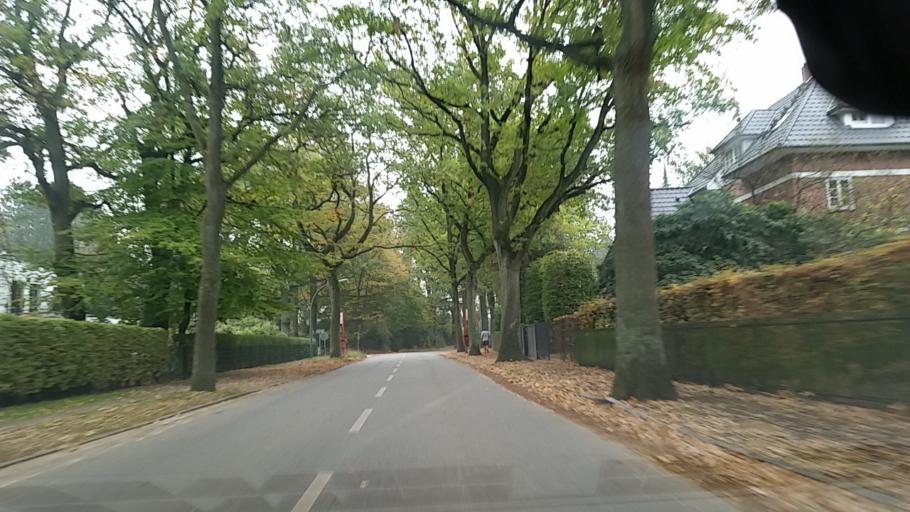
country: DE
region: Schleswig-Holstein
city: Halstenbek
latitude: 53.5574
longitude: 9.8371
